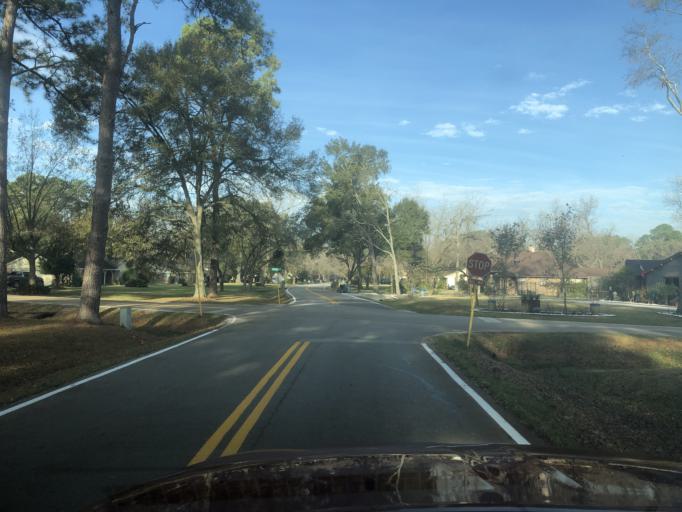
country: US
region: Texas
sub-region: Harris County
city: Spring
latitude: 30.0109
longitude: -95.4721
